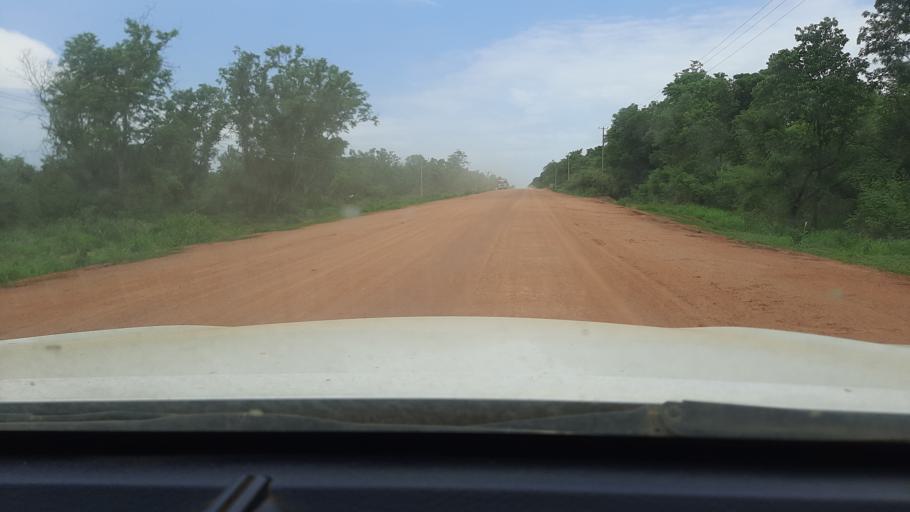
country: ET
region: Gambela
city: Gambela
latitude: 8.1435
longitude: 34.5766
